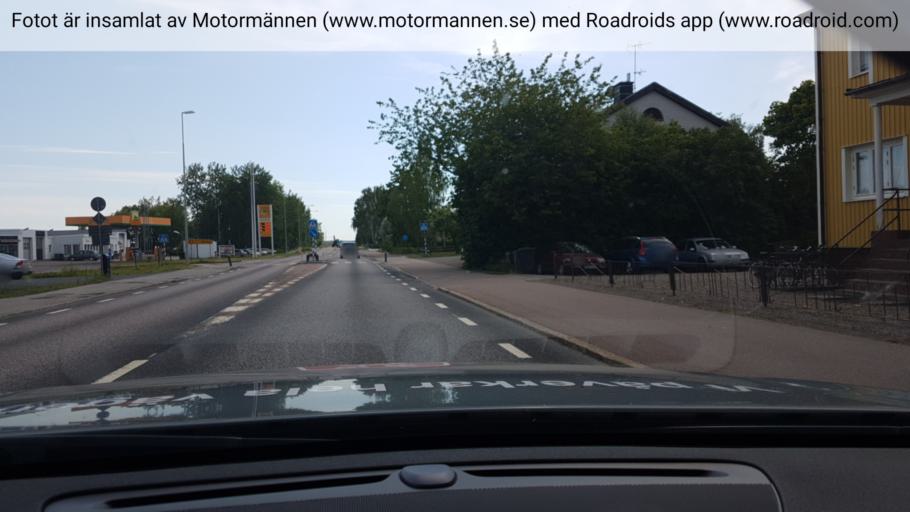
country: SE
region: Uppsala
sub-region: Osthammars Kommun
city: Gimo
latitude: 60.1697
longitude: 18.1936
